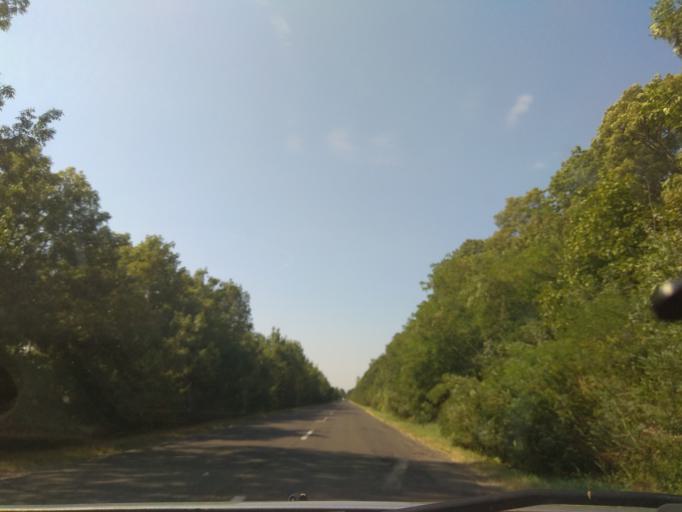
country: HU
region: Borsod-Abauj-Zemplen
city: Harsany
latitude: 47.9289
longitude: 20.7275
